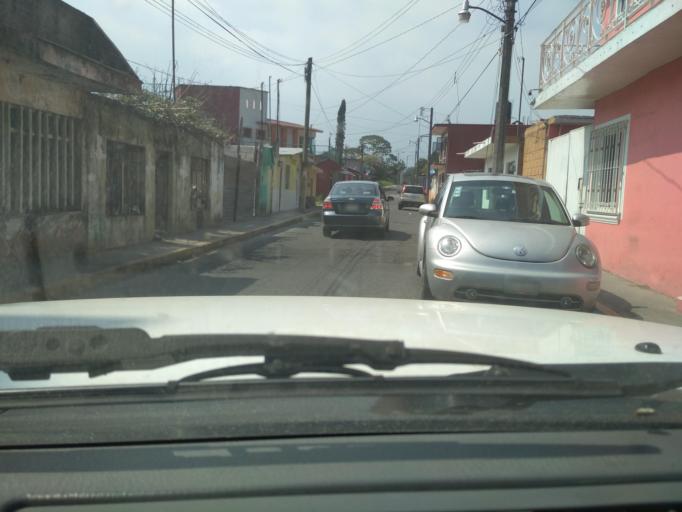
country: MX
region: Veracruz
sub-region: Mariano Escobedo
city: Palmira
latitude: 18.8743
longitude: -97.0984
